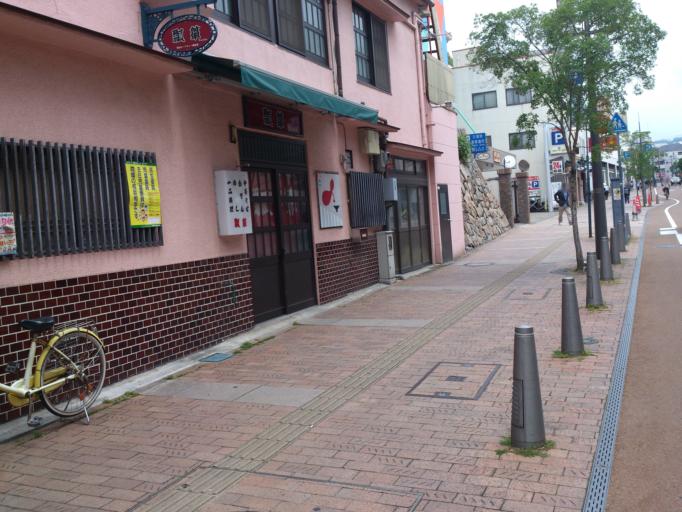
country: JP
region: Ehime
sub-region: Shikoku-chuo Shi
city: Matsuyama
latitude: 33.8433
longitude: 132.7711
